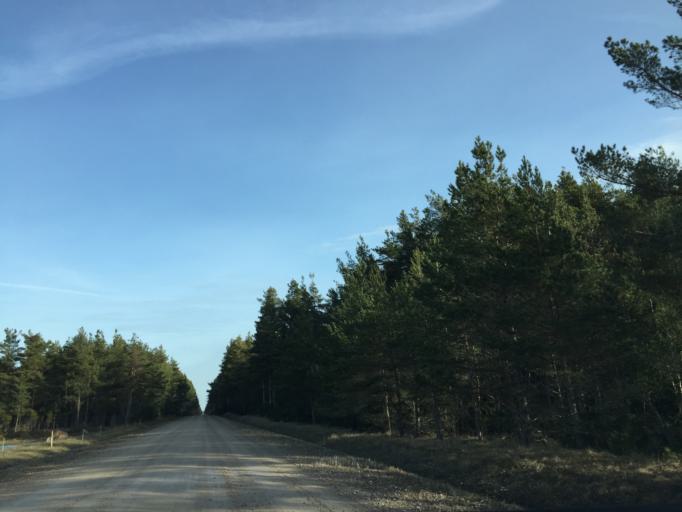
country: EE
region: Saare
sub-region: Kuressaare linn
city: Kuressaare
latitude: 58.2859
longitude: 21.9276
